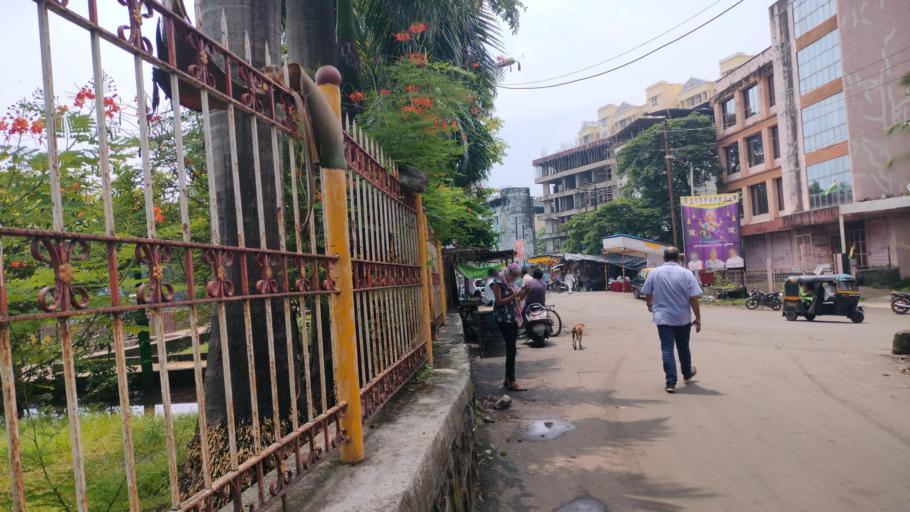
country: IN
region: Maharashtra
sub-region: Thane
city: Virar
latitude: 19.4106
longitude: 72.8281
